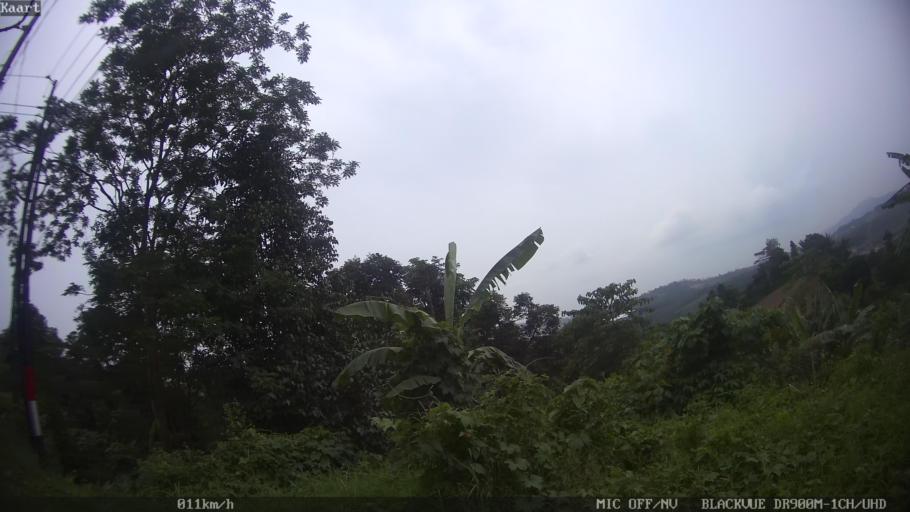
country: ID
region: Lampung
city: Panjang
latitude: -5.4363
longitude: 105.3128
